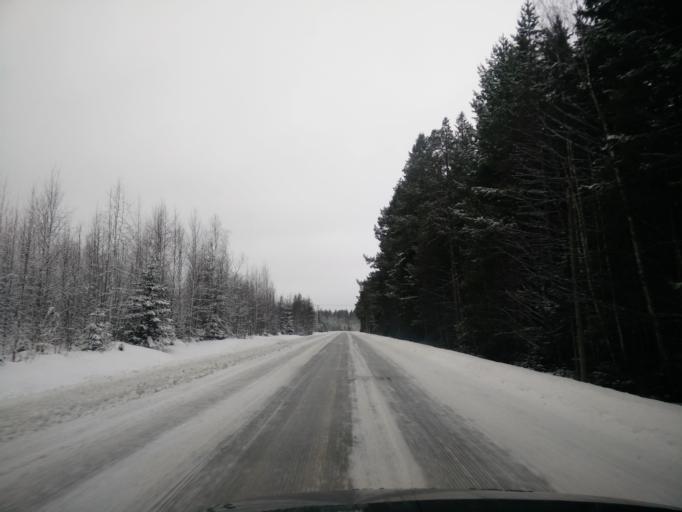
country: SE
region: Vaesternorrland
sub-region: Ange Kommun
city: Ange
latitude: 62.3972
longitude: 15.3602
